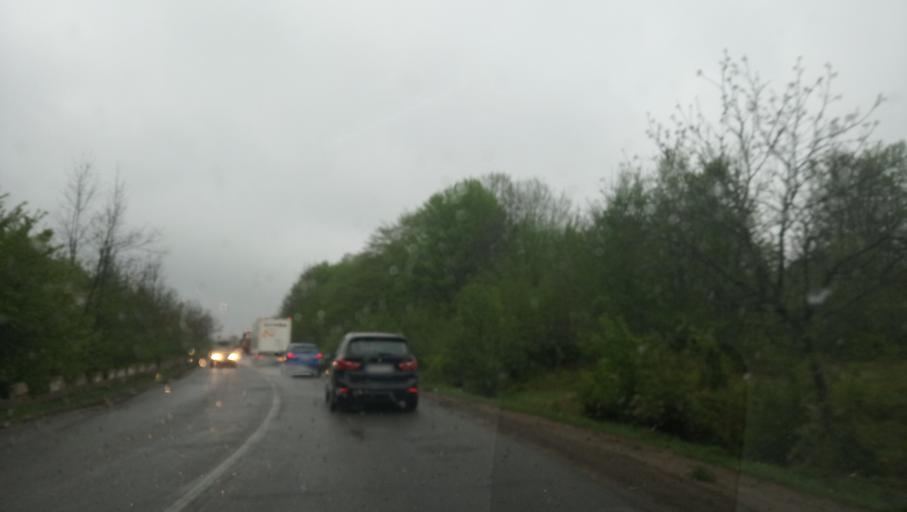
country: RO
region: Timis
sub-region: Comuna Pietroasa
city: Pietroasa
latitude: 45.8856
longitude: 22.4235
